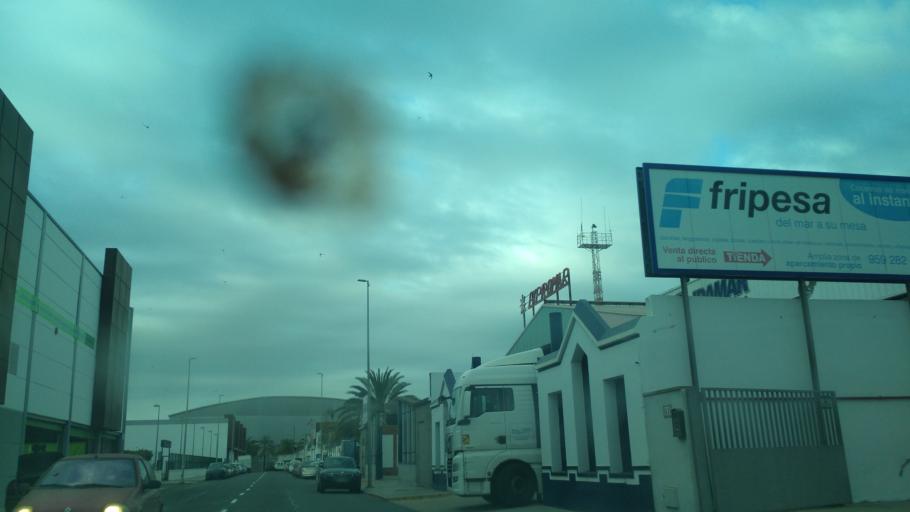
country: ES
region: Andalusia
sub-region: Provincia de Huelva
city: Huelva
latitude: 37.2645
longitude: -6.9596
